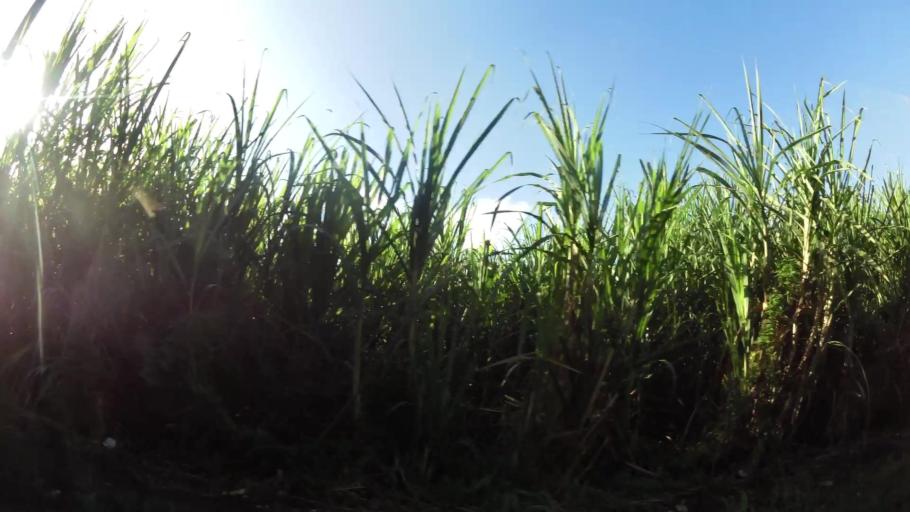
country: MQ
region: Martinique
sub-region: Martinique
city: Le Lamentin
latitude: 14.6337
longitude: -61.0326
